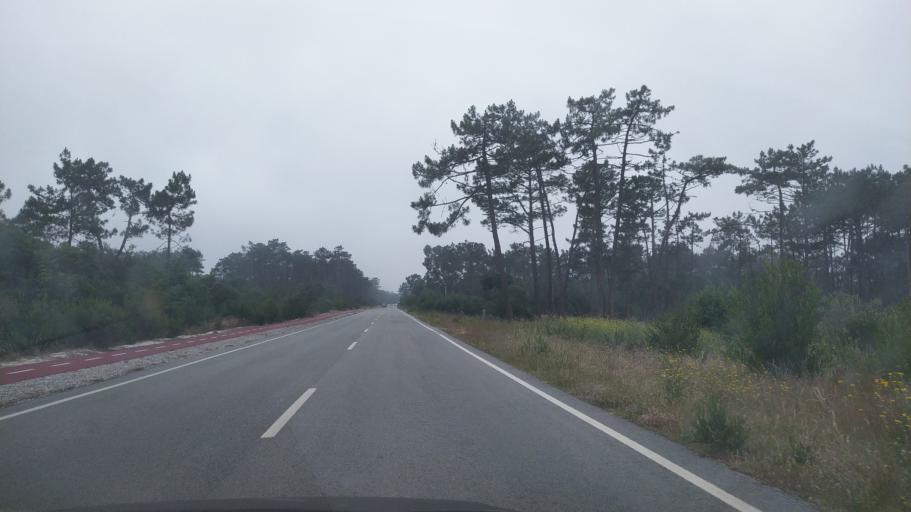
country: PT
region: Aveiro
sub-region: Ilhavo
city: Gafanha da Encarnacao
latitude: 40.5686
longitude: -8.7387
